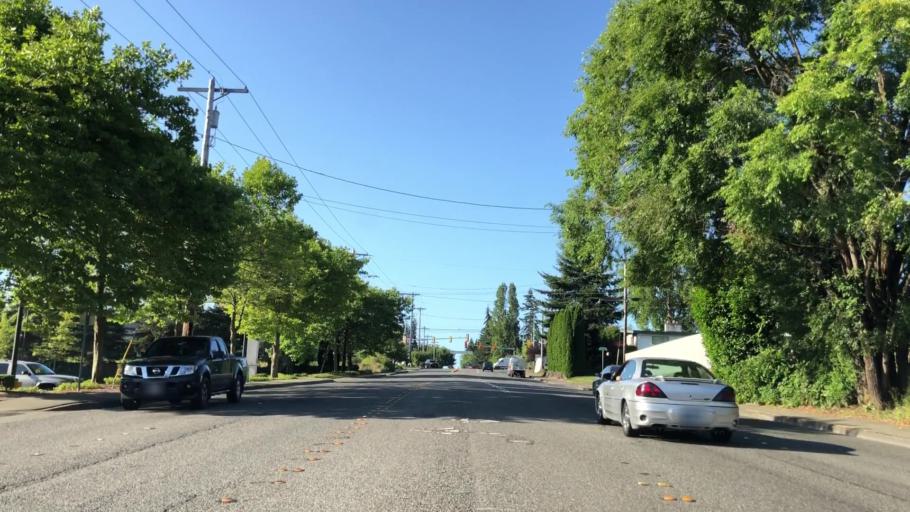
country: US
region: Washington
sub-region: Snohomish County
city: Alderwood Manor
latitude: 47.8082
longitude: -122.2923
